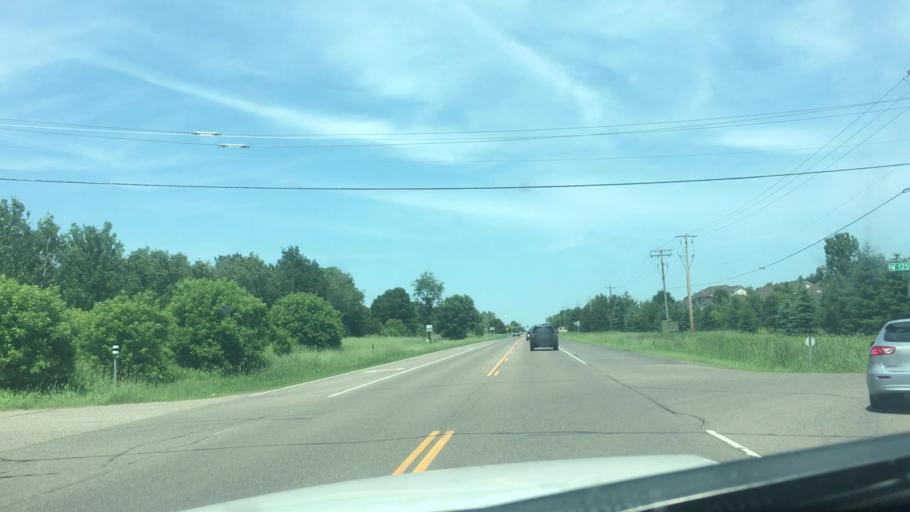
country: US
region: Minnesota
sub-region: Washington County
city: Hugo
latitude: 45.1309
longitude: -93.0018
